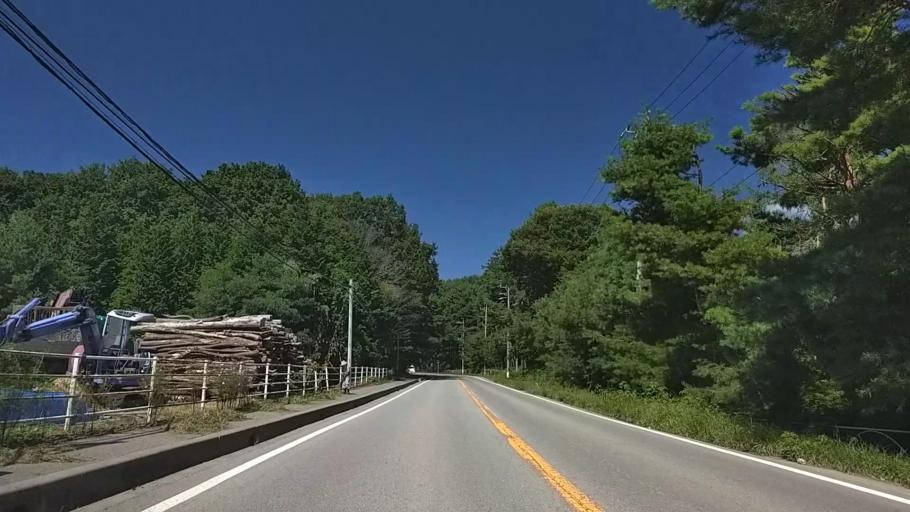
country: JP
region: Nagano
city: Komoro
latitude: 36.3363
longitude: 138.5086
